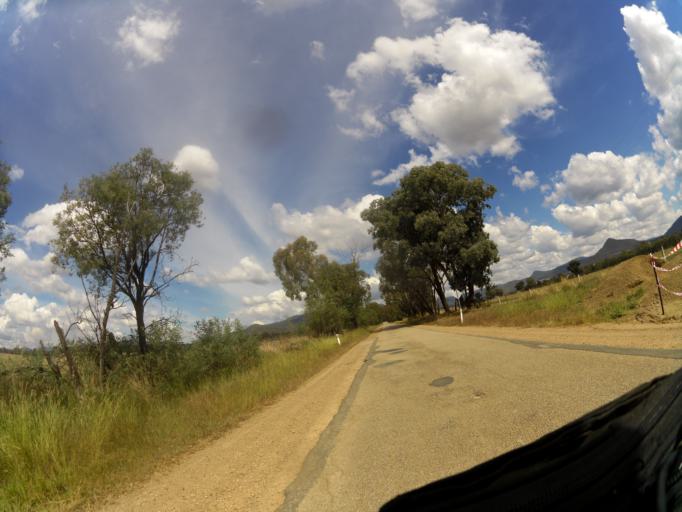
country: AU
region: Victoria
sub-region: Benalla
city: Benalla
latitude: -36.7566
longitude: 145.9781
